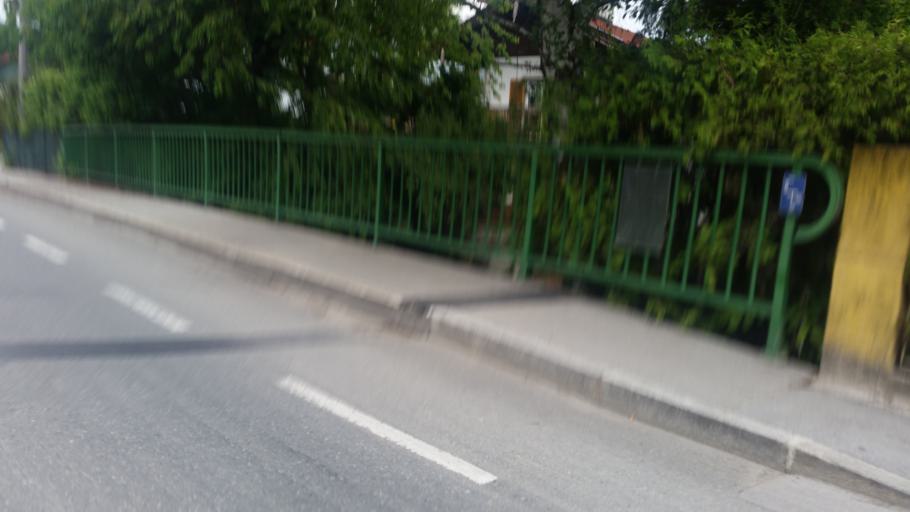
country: AT
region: Salzburg
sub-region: Politischer Bezirk Salzburg-Umgebung
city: Bergheim
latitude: 47.8253
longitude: 13.0578
